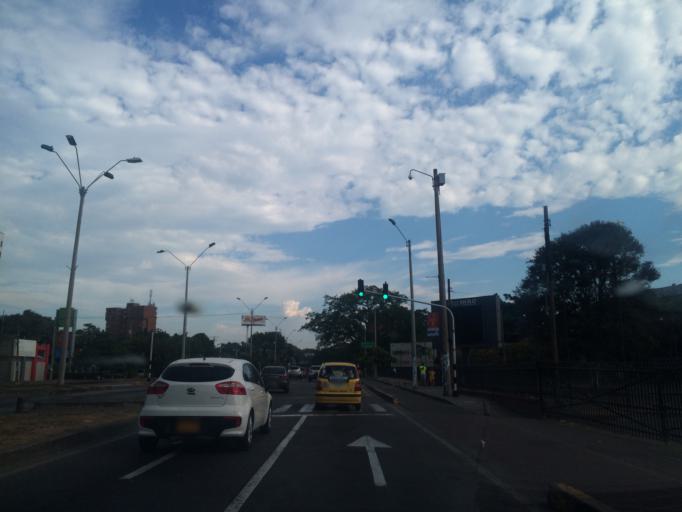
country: CO
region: Valle del Cauca
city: Cali
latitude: 3.4119
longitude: -76.5479
